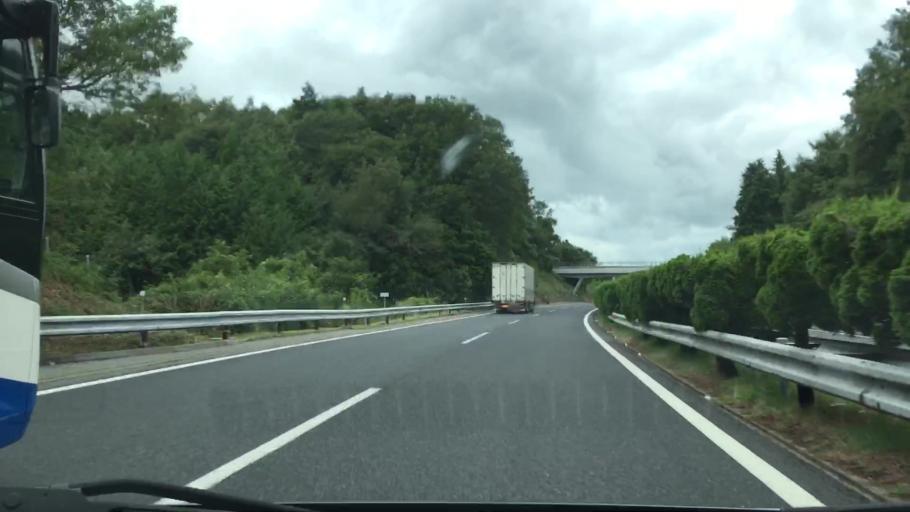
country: JP
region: Okayama
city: Tsuyama
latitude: 35.0360
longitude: 134.1344
